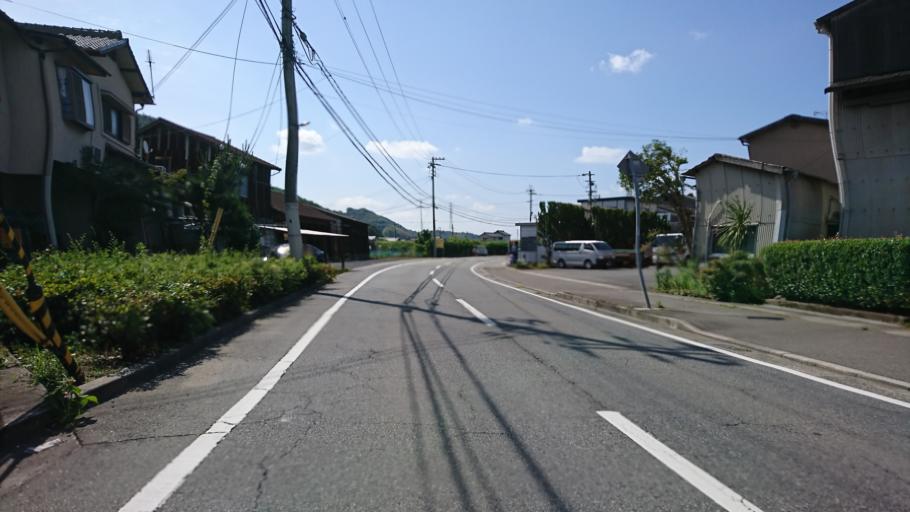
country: JP
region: Hyogo
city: Shirahamacho-usazakiminami
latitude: 34.7932
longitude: 134.7487
